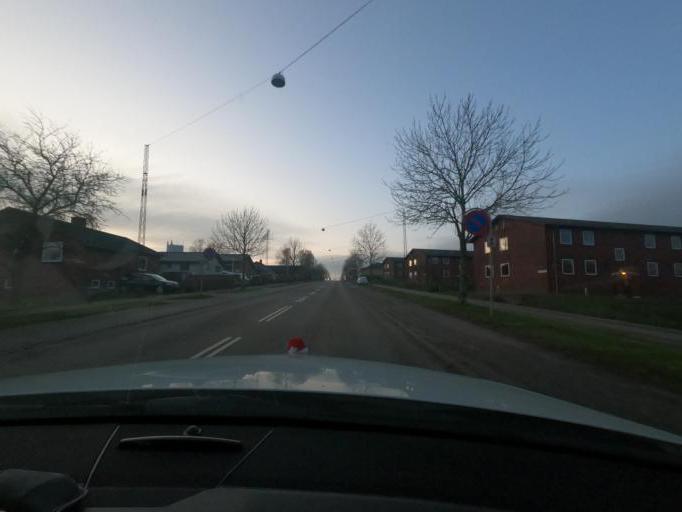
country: DK
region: South Denmark
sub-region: Sonderborg Kommune
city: Sonderborg
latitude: 54.9189
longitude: 9.7925
